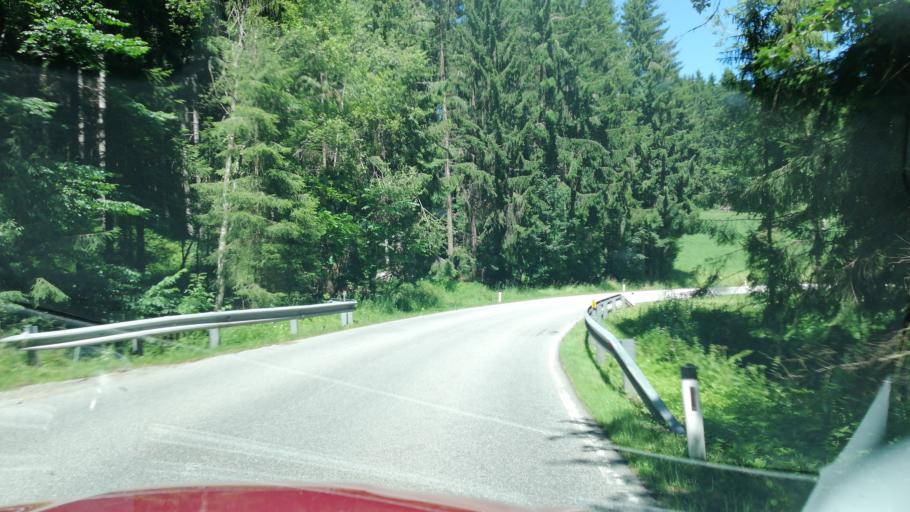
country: AT
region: Upper Austria
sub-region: Politischer Bezirk Urfahr-Umgebung
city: Haibach im Muhlkreis
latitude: 48.4399
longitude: 14.3558
